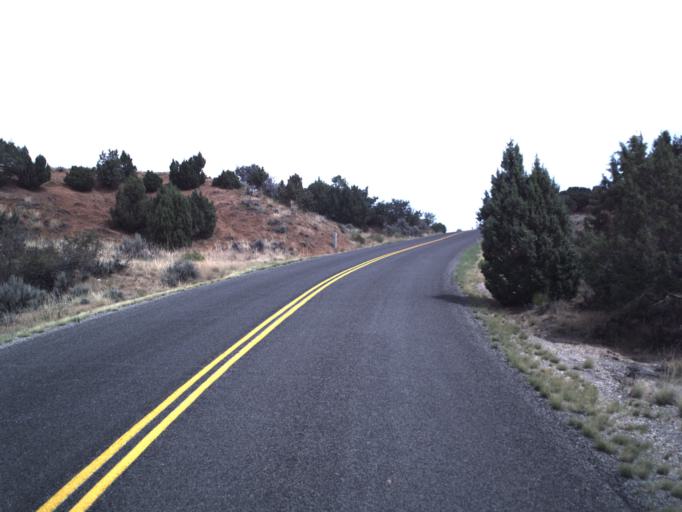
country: US
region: Utah
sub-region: Uintah County
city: Maeser
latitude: 40.5256
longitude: -109.5372
